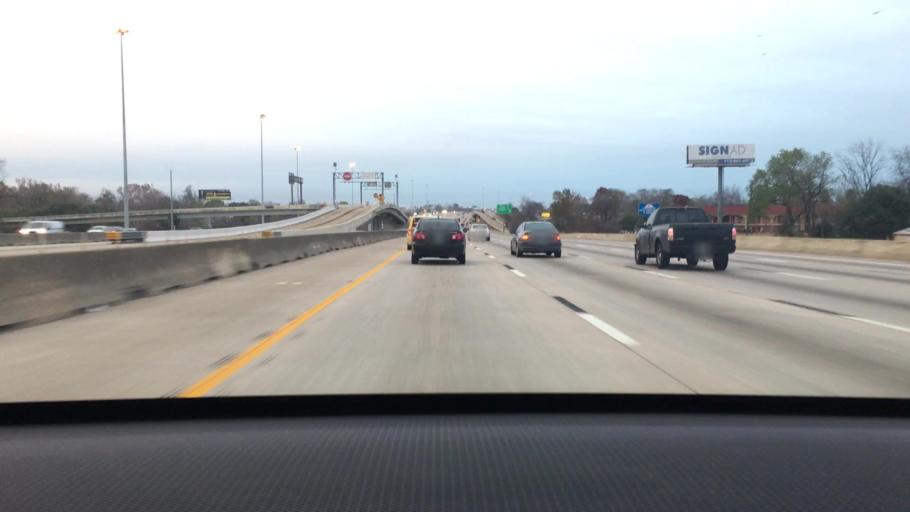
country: US
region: Texas
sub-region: Harris County
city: Houston
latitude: 29.8492
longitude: -95.3335
